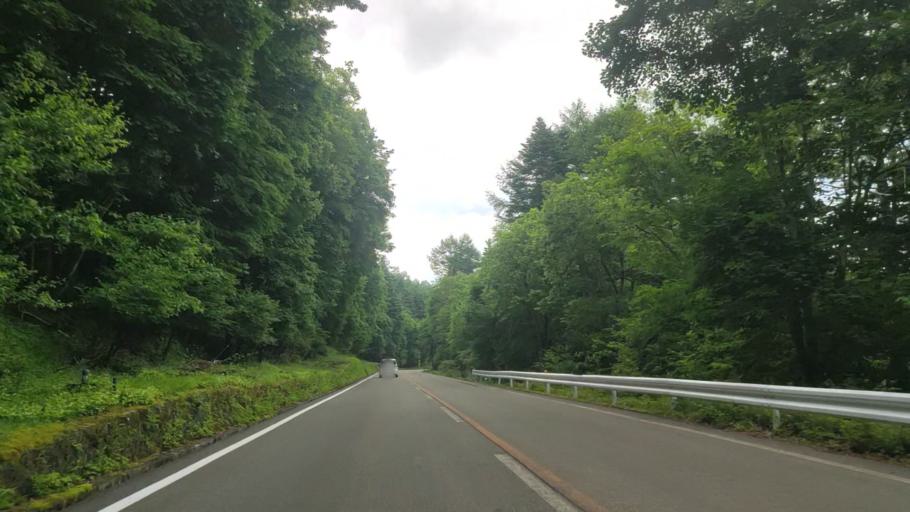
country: JP
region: Yamanashi
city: Fujikawaguchiko
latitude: 35.4143
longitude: 138.7339
